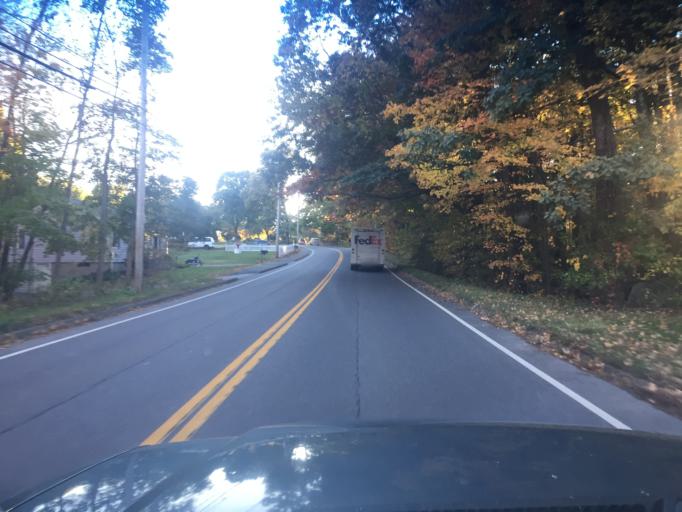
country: US
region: Massachusetts
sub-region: Middlesex County
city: Hudson
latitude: 42.3917
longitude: -71.5412
